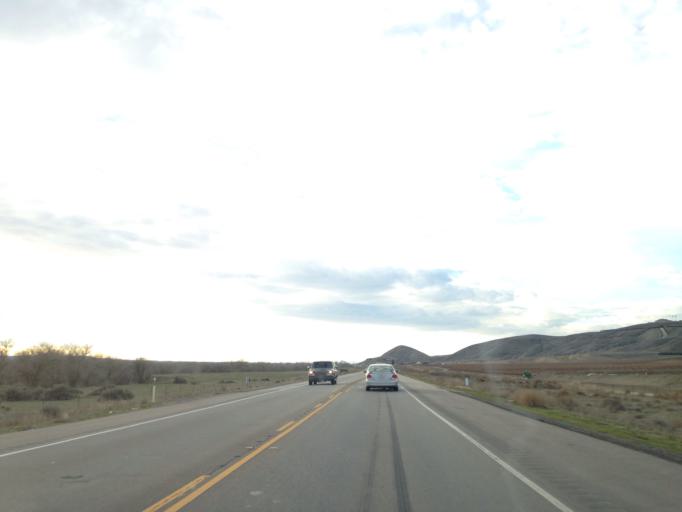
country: US
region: California
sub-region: San Luis Obispo County
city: Shandon
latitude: 35.6625
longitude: -120.3839
